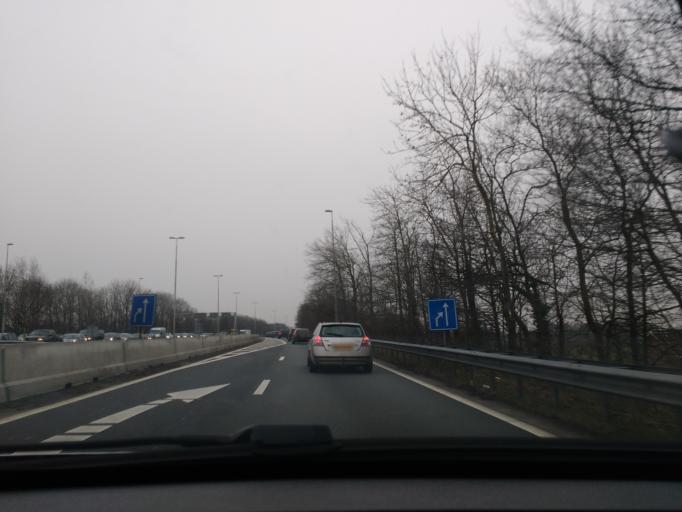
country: NL
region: Gelderland
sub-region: Gemeente Barneveld
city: Barneveld
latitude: 52.1648
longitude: 5.5658
